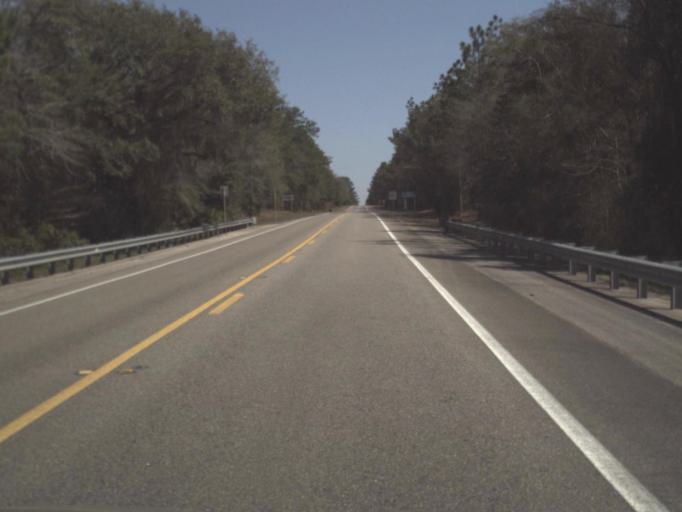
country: US
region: Florida
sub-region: Liberty County
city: Bristol
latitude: 30.5204
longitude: -84.8168
